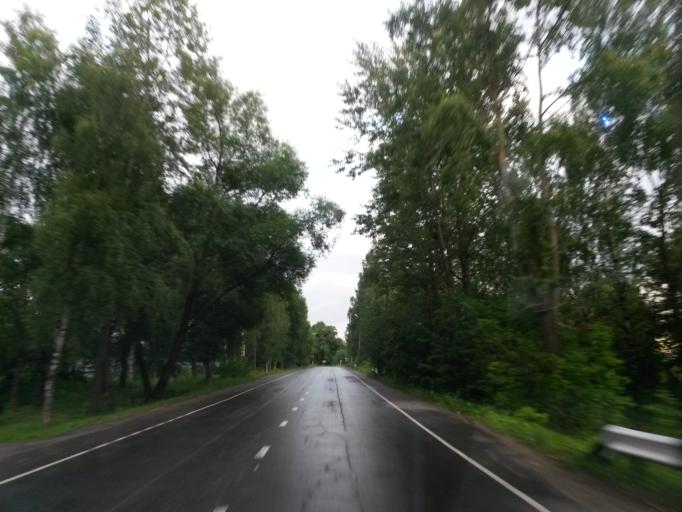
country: RU
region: Jaroslavl
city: Tutayev
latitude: 57.8944
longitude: 39.5282
